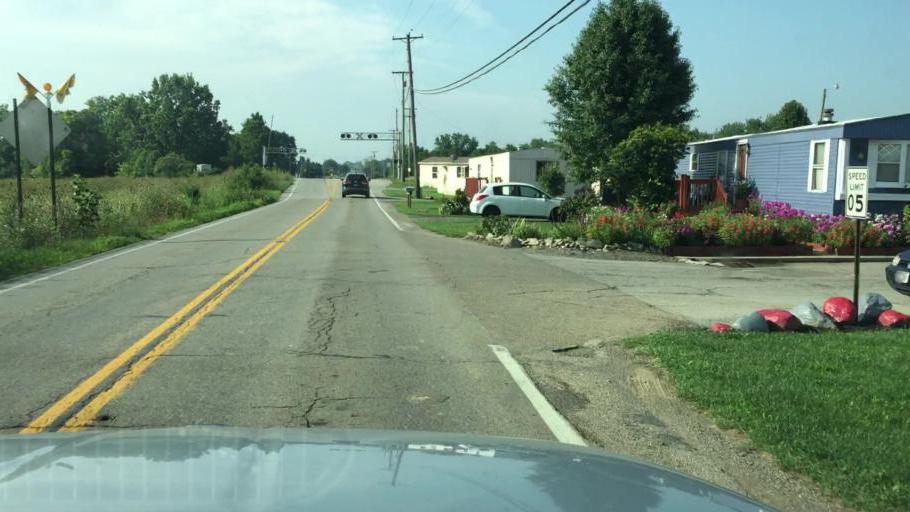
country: US
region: Ohio
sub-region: Franklin County
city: Hilliard
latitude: 40.0590
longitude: -83.1604
